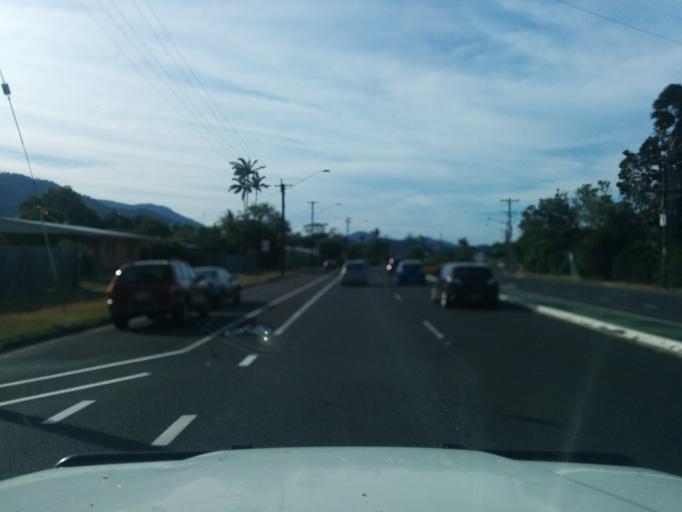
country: AU
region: Queensland
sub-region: Cairns
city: Woree
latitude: -16.9354
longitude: 145.7441
